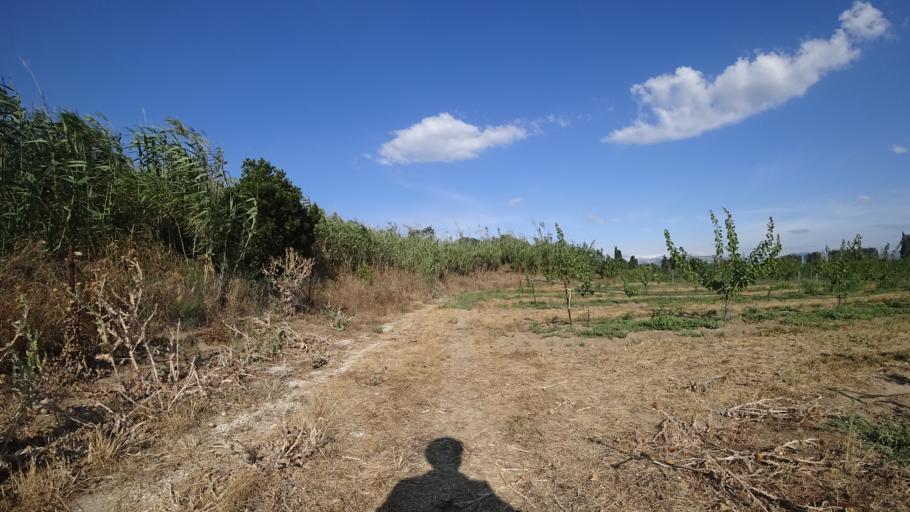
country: FR
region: Languedoc-Roussillon
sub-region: Departement des Pyrenees-Orientales
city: Rivesaltes
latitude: 42.7734
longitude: 2.8882
